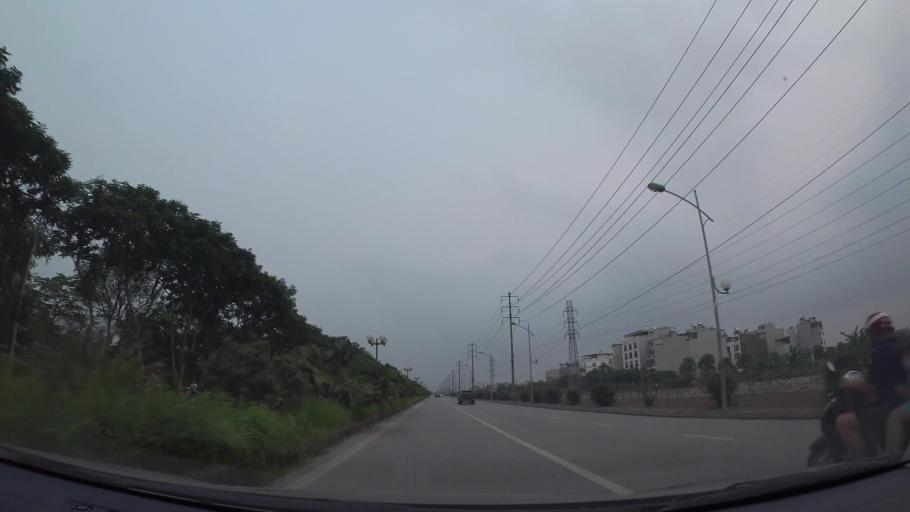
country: VN
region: Ha Noi
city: Trau Quy
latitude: 21.0603
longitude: 105.9025
